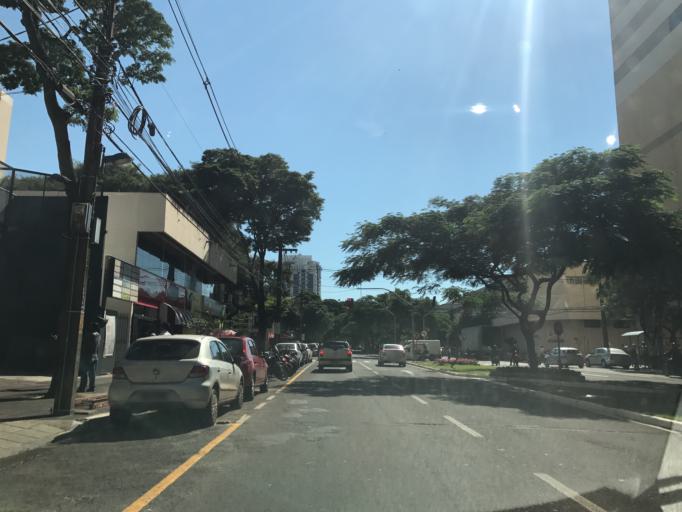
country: BR
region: Parana
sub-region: Maringa
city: Maringa
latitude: -23.4225
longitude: -51.9331
